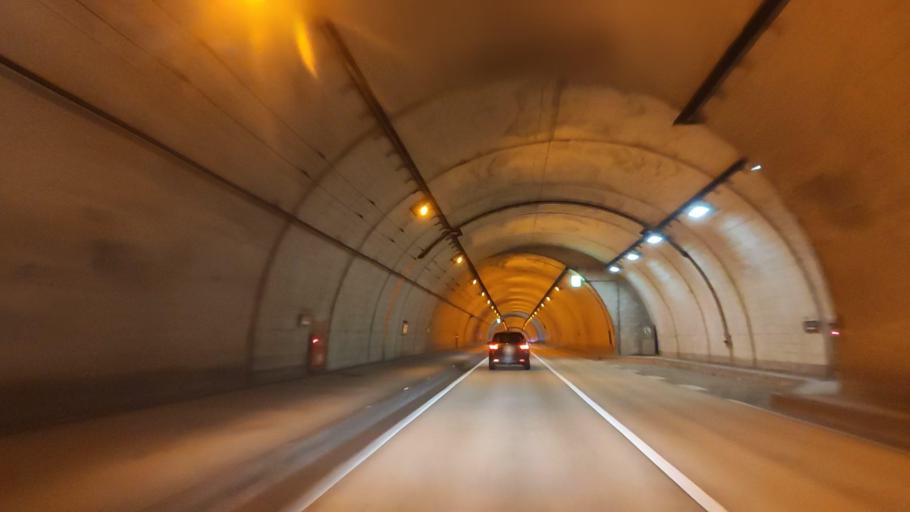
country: JP
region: Ehime
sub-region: Shikoku-chuo Shi
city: Matsuyama
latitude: 33.8806
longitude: 132.7114
